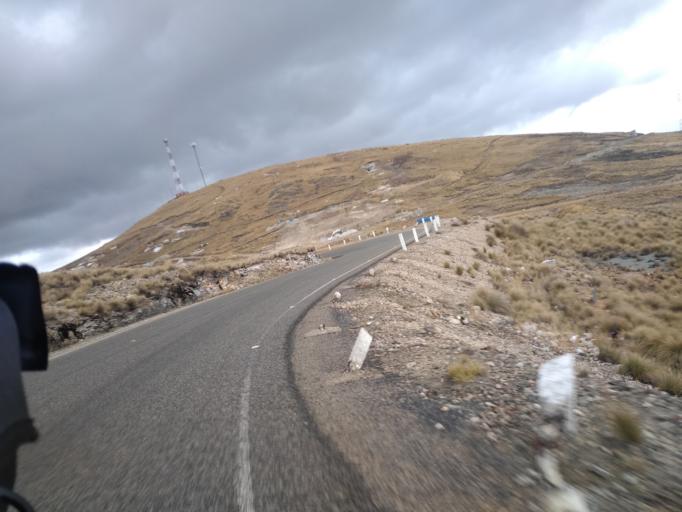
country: PE
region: La Libertad
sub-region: Provincia de Santiago de Chuco
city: Quiruvilca
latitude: -7.9956
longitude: -78.3092
